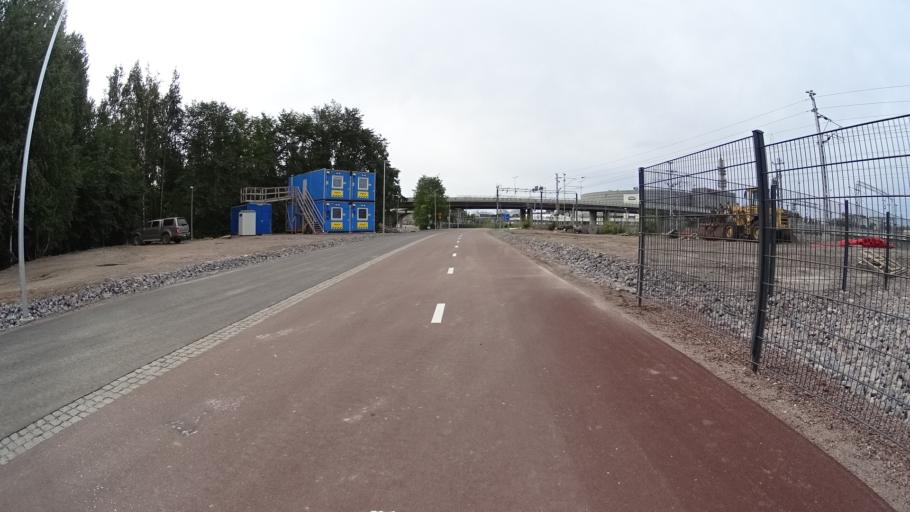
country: FI
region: Uusimaa
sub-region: Helsinki
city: Helsinki
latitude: 60.2080
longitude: 24.9342
